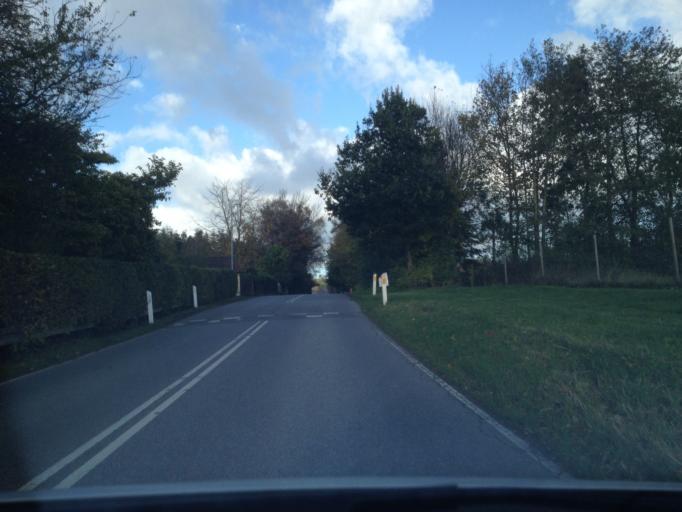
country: DK
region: Capital Region
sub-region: Fureso Kommune
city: Farum
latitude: 55.8369
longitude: 12.3760
